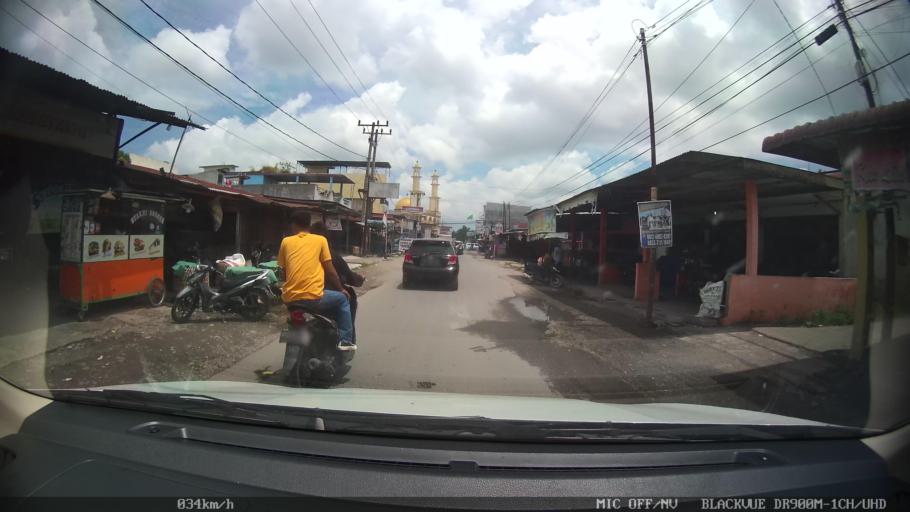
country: ID
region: North Sumatra
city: Medan
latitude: 3.6195
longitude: 98.7483
